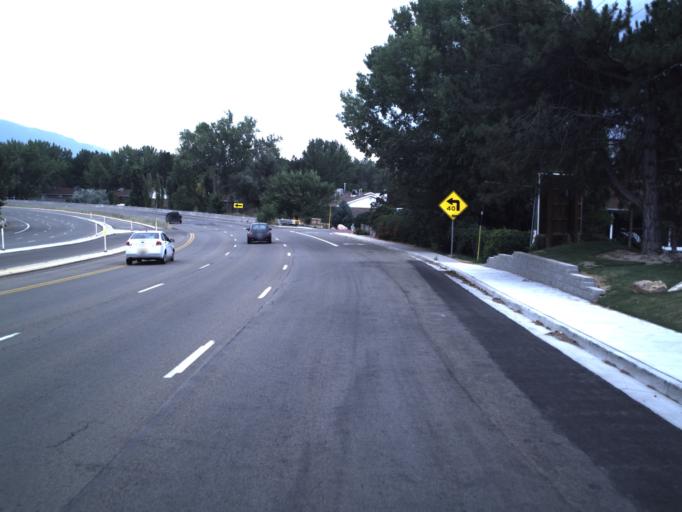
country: US
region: Utah
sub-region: Salt Lake County
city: Murray
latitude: 40.6699
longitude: -111.8717
